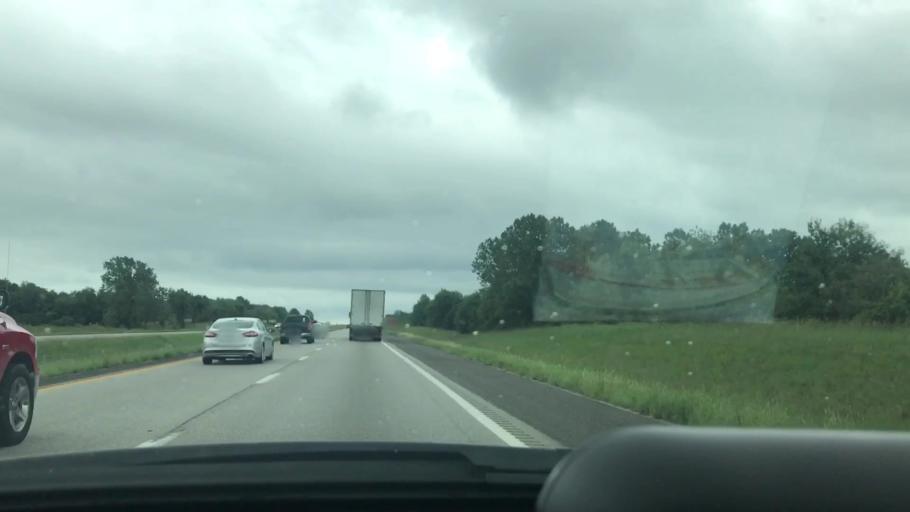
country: US
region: Missouri
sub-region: Christian County
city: Billings
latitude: 37.1864
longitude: -93.6046
